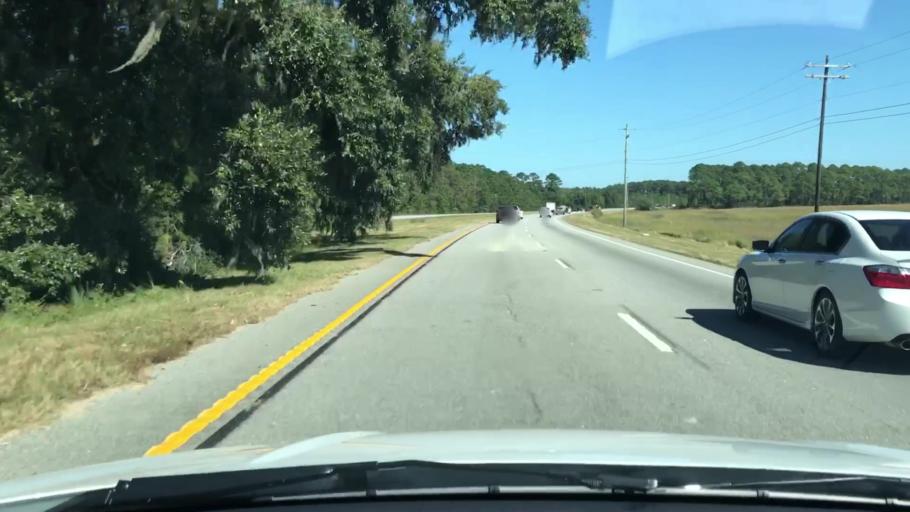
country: US
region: South Carolina
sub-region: Beaufort County
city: Laurel Bay
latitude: 32.3721
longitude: -80.8516
